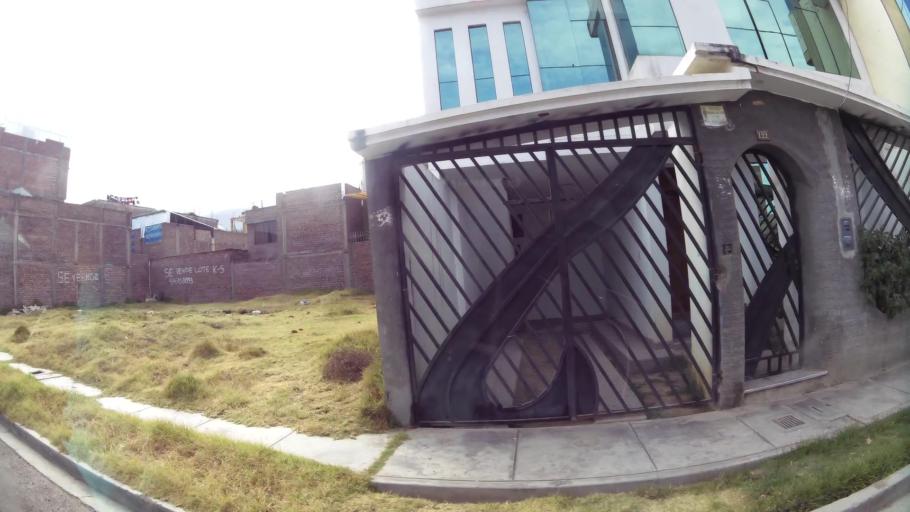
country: PE
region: Junin
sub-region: Provincia de Huancayo
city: Huancayo
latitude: -12.0491
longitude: -75.1943
